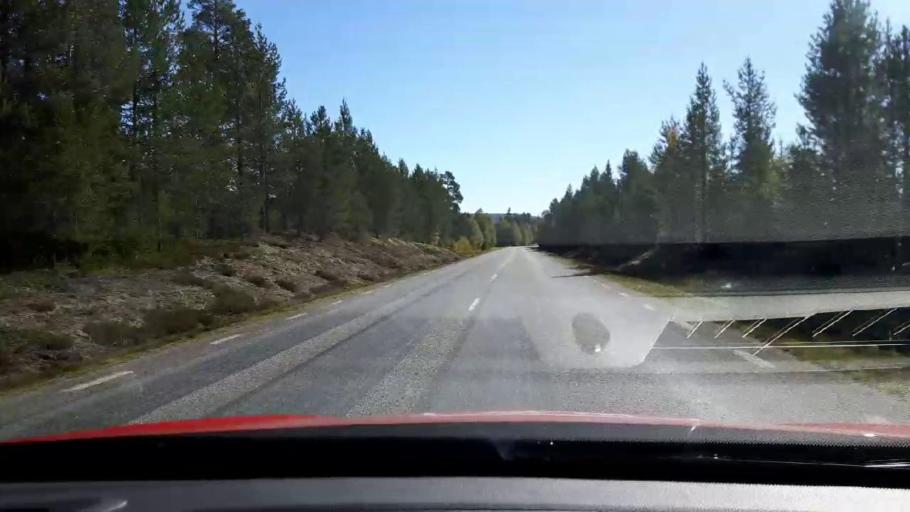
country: SE
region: Jaemtland
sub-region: Harjedalens Kommun
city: Sveg
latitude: 62.3539
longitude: 14.0227
